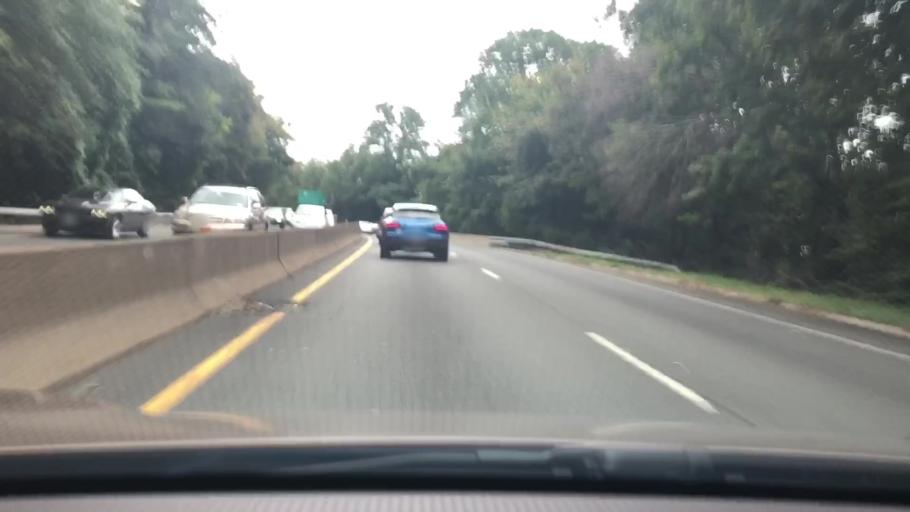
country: US
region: New York
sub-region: Westchester County
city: Pelham Manor
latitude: 40.8961
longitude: -73.8167
